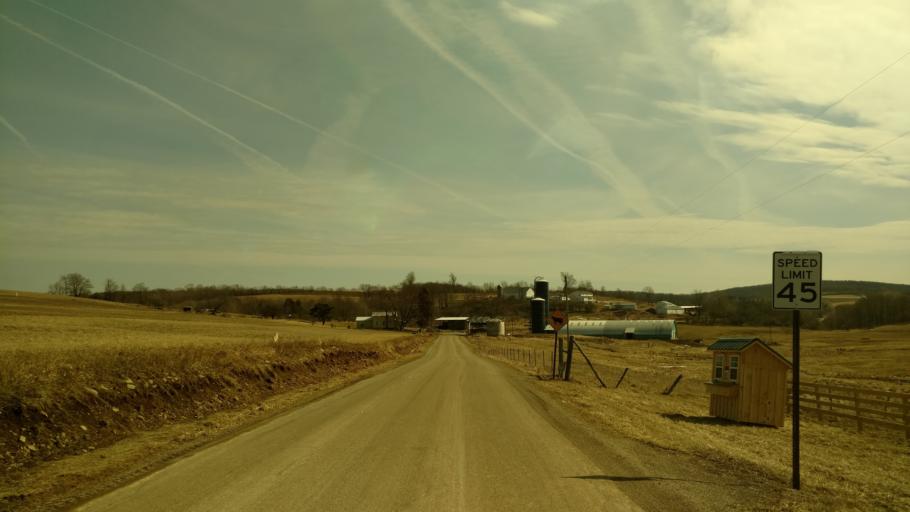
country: US
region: Pennsylvania
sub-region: Tioga County
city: Westfield
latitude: 41.9247
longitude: -77.7628
